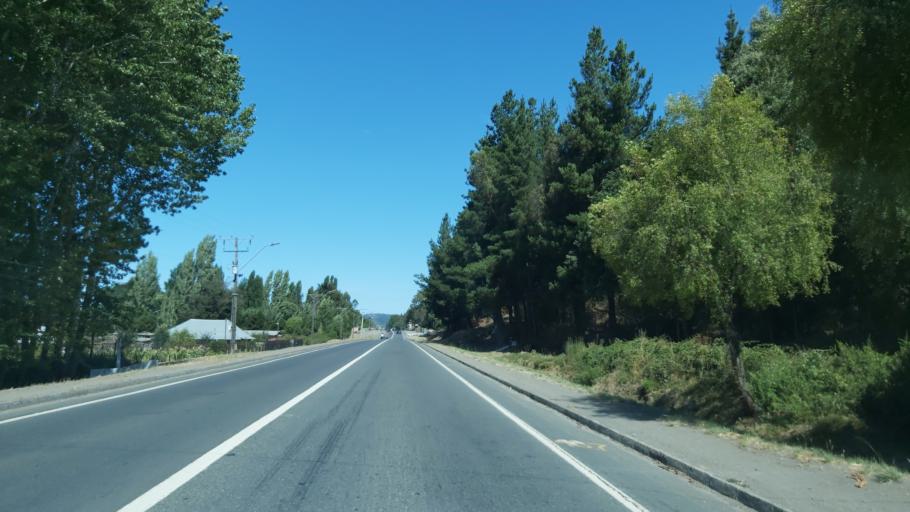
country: CL
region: Biobio
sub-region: Provincia de Concepcion
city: Lota
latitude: -37.1551
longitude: -72.9710
